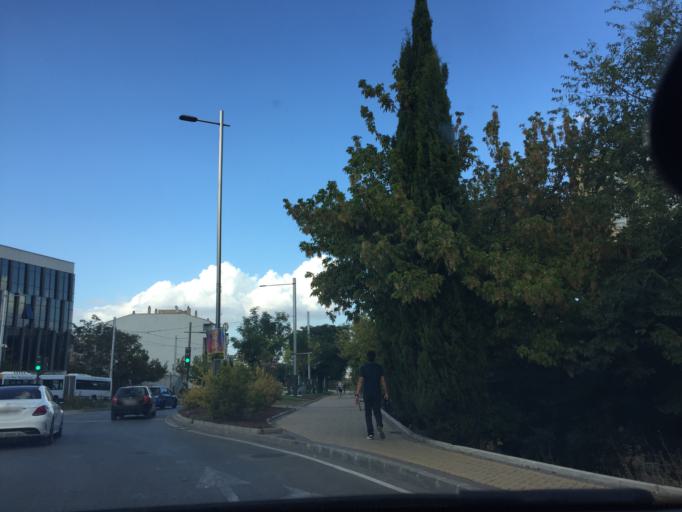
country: ES
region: Andalusia
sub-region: Provincia de Jaen
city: Jaen
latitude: 37.7796
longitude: -3.7845
